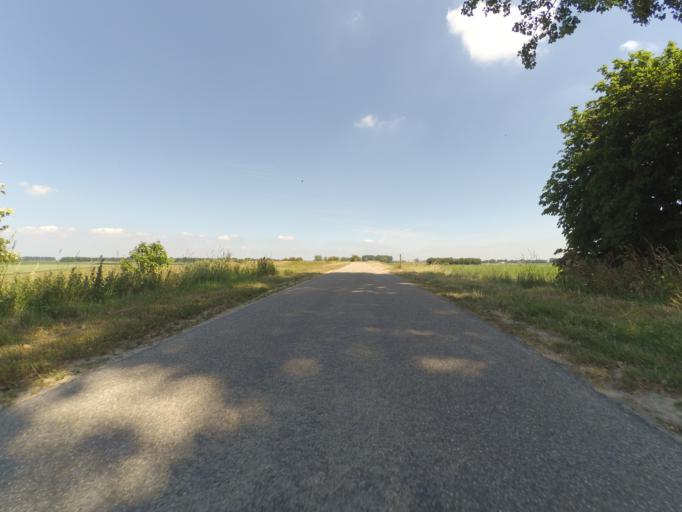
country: NL
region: Zeeland
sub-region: Gemeente Reimerswaal
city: Yerseke
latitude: 51.5688
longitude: 4.0373
